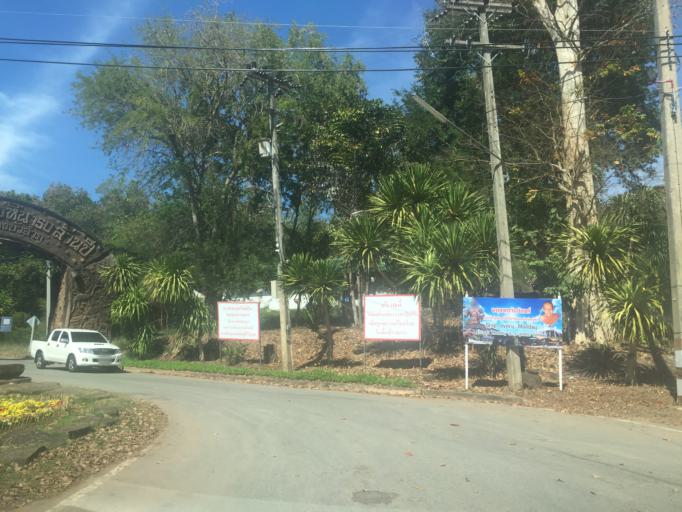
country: TH
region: Changwat Nong Bua Lamphu
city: Nong Bua Lamphu
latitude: 17.2437
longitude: 102.5195
